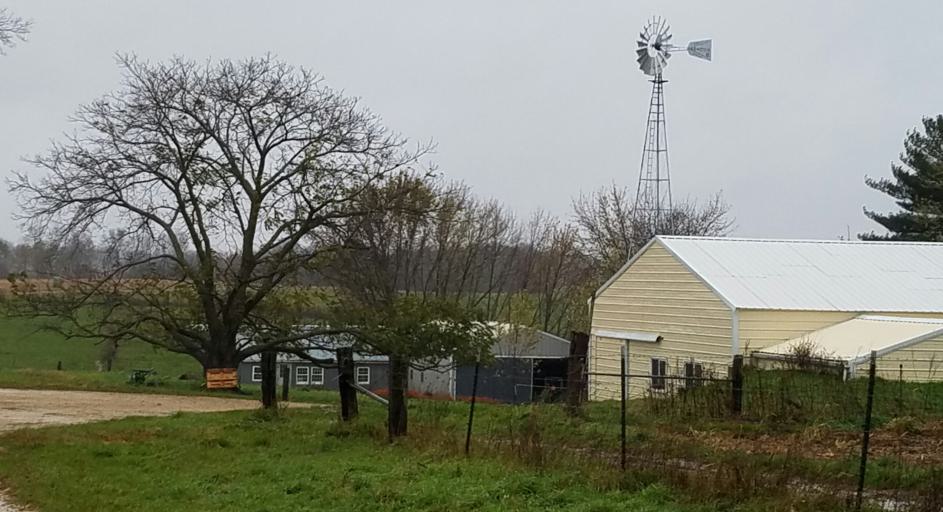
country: US
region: Wisconsin
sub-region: Vernon County
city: Hillsboro
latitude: 43.5813
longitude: -90.3818
